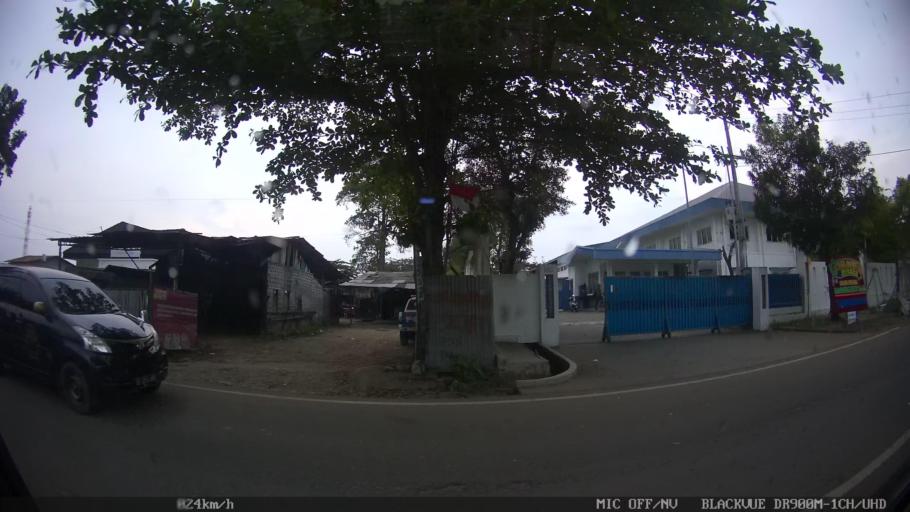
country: ID
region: Lampung
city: Kedaton
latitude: -5.3950
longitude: 105.2813
